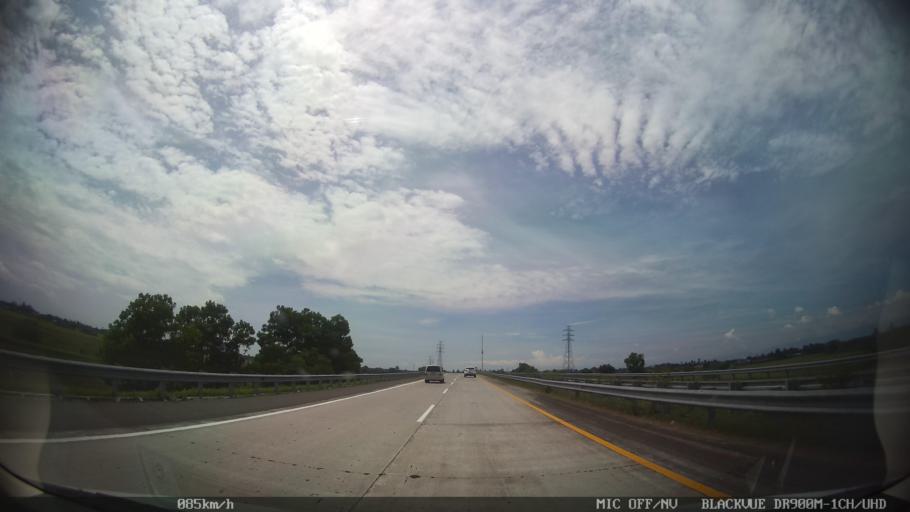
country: ID
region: North Sumatra
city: Percut
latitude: 3.5484
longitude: 98.8525
